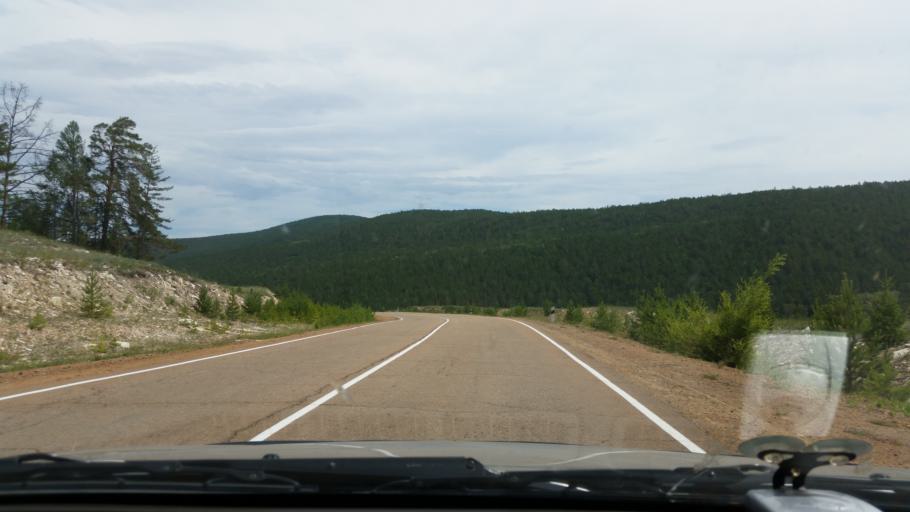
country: RU
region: Irkutsk
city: Yelantsy
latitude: 52.7655
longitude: 106.3510
